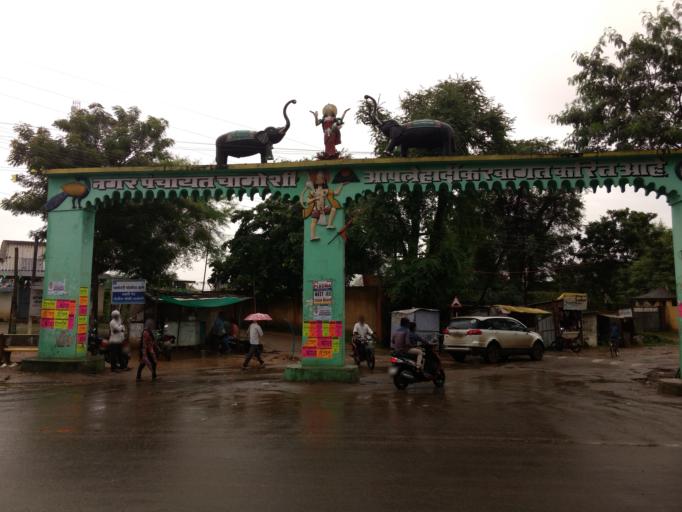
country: IN
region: Maharashtra
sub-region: Chandrapur
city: Mul
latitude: 19.9390
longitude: 79.8909
